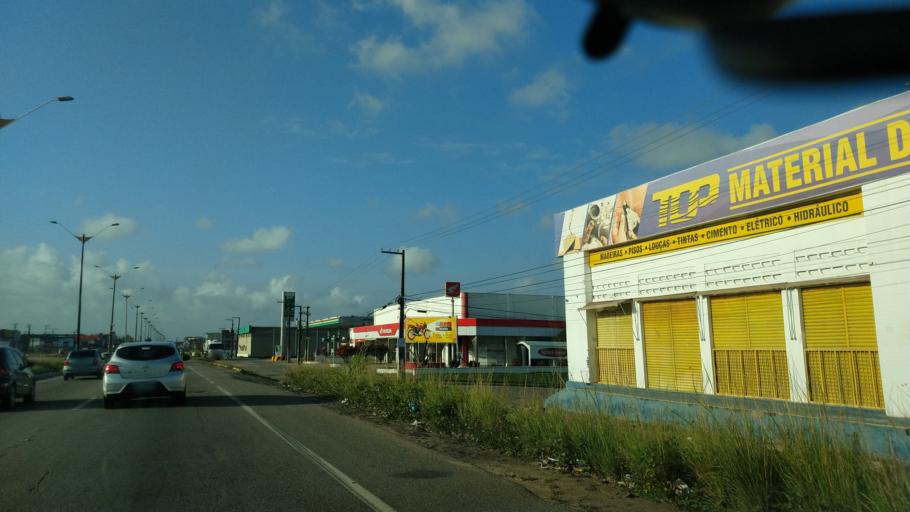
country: BR
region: Rio Grande do Norte
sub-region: Parnamirim
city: Parnamirim
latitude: -5.9032
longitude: -35.2597
